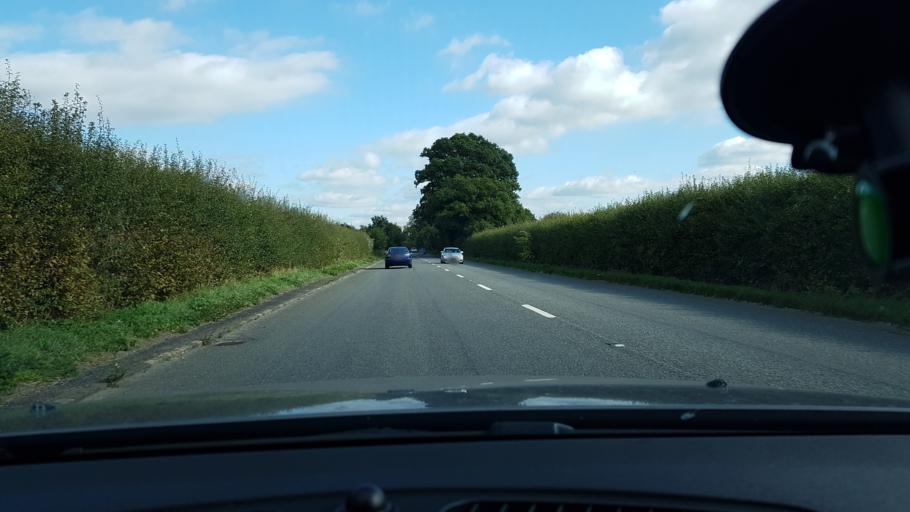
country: GB
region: England
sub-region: West Berkshire
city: Kintbury
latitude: 51.4134
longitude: -1.4620
